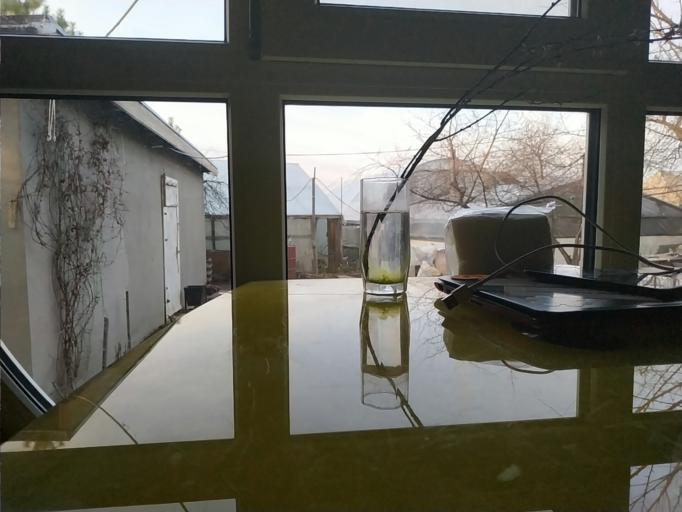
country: RU
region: Republic of Karelia
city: Suoyarvi
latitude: 62.3571
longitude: 32.0465
